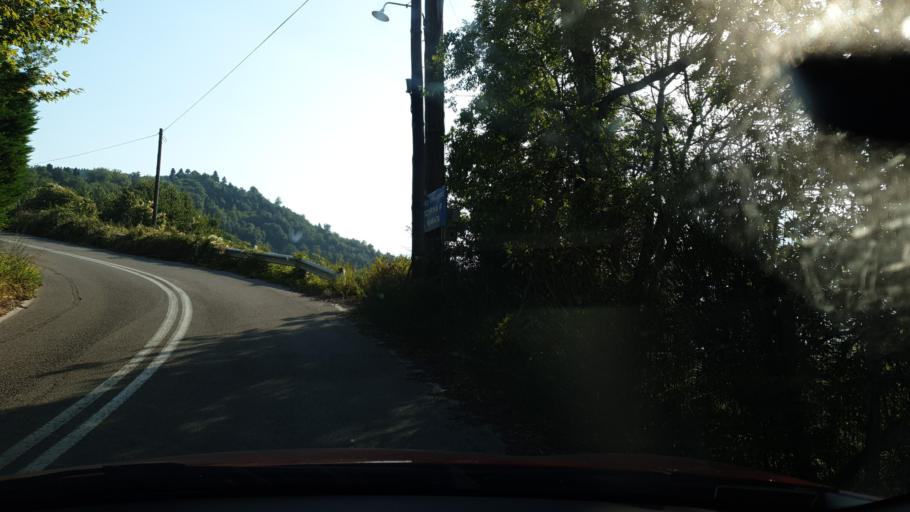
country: GR
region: Central Greece
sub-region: Nomos Evvoias
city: Kymi
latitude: 38.6456
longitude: 23.9387
